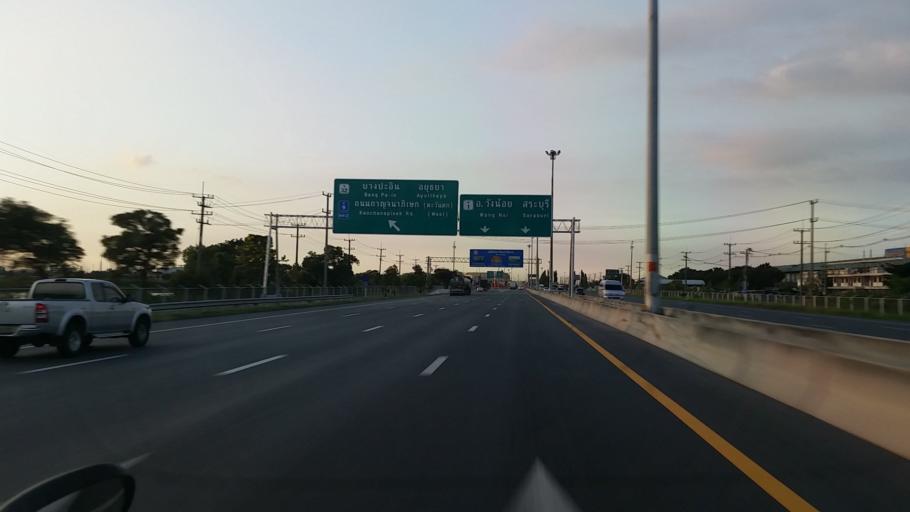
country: TH
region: Phra Nakhon Si Ayutthaya
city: Bang Pa-in
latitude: 14.1802
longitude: 100.6418
